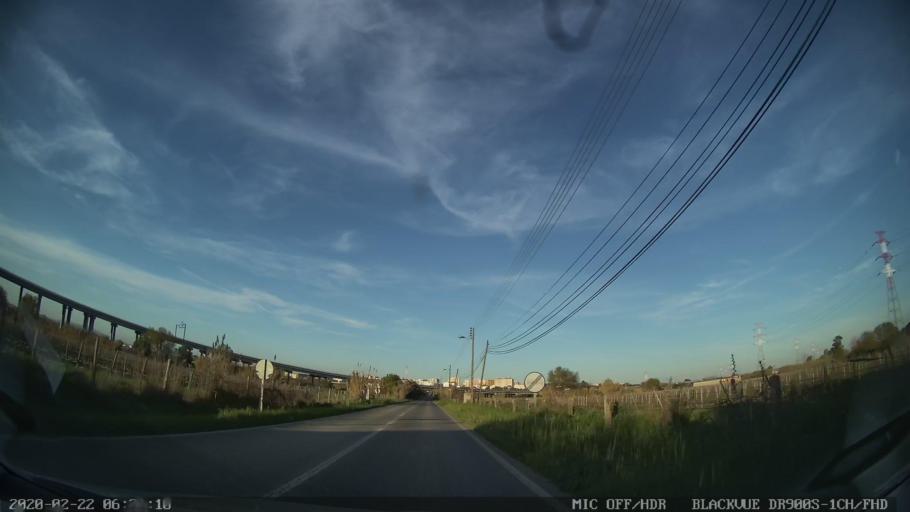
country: PT
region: Lisbon
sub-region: Alenquer
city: Carregado
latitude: 39.0150
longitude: -8.9823
